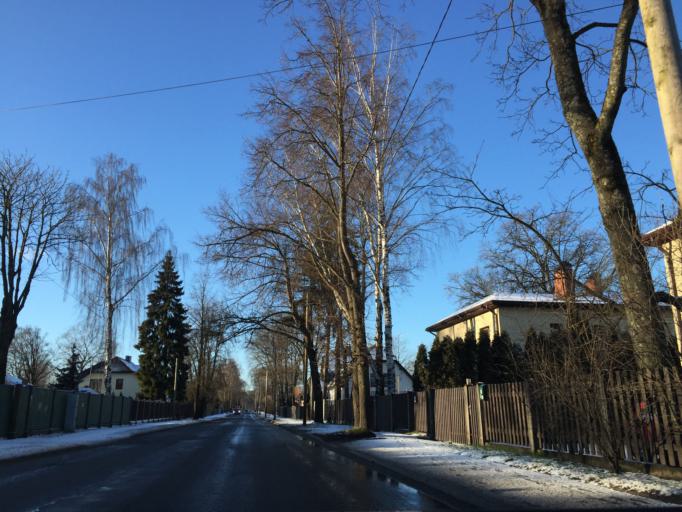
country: LV
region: Marupe
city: Marupe
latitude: 56.9124
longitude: 24.0744
